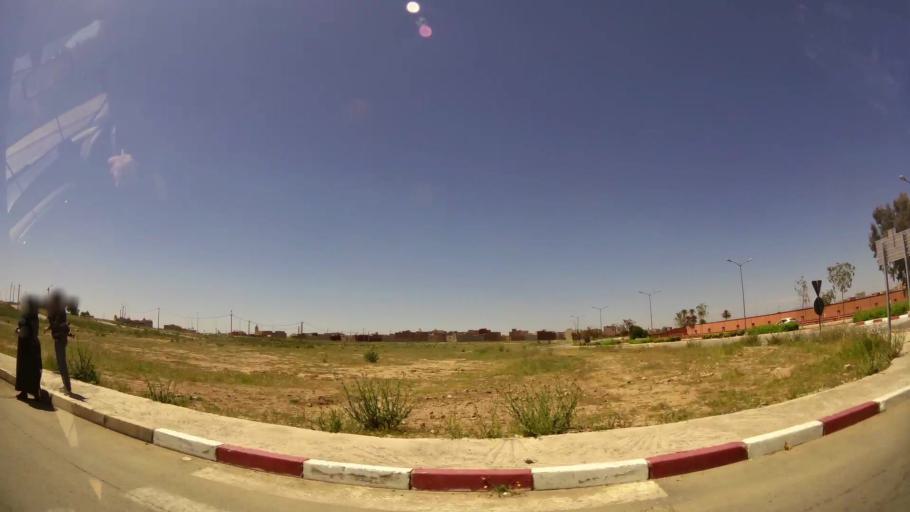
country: MA
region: Oriental
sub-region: Oujda-Angad
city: Oujda
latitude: 34.6672
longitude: -1.8636
